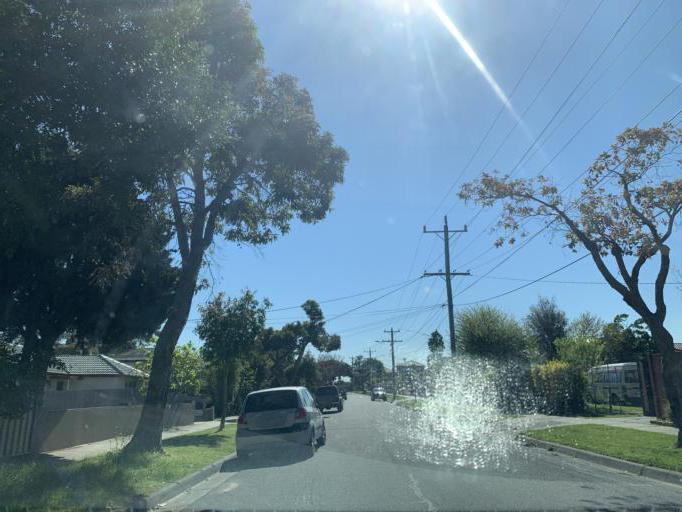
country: AU
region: Victoria
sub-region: Greater Dandenong
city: Dandenong
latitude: -37.9972
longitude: 145.2001
